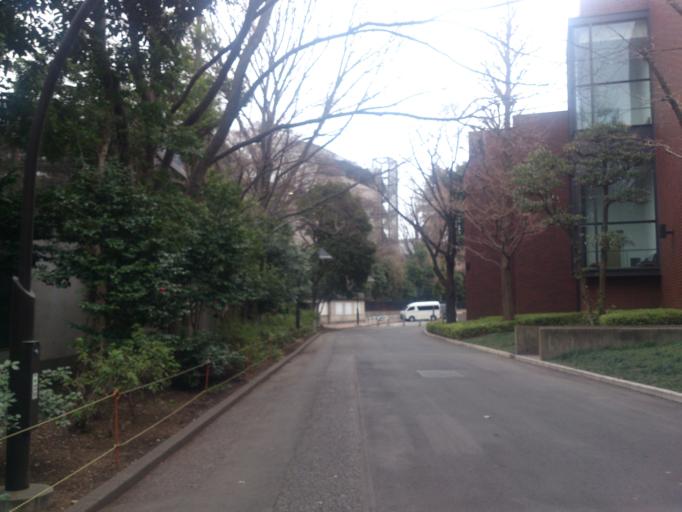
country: JP
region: Tokyo
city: Tokyo
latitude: 35.7174
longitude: 139.7725
